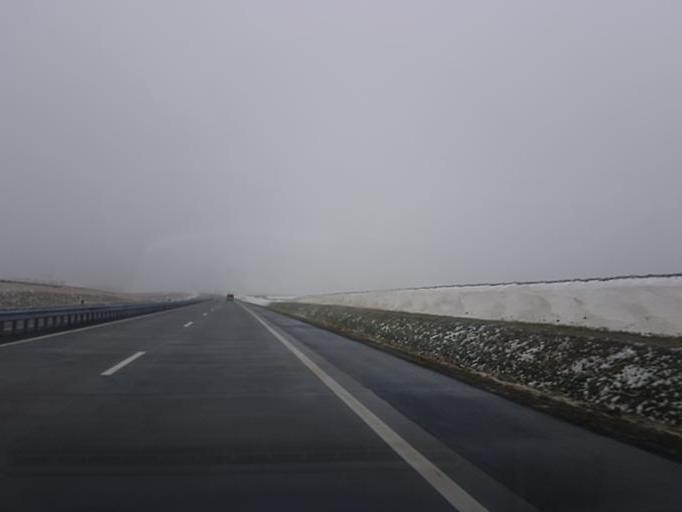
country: BY
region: Minsk
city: Atolina
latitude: 53.7435
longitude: 27.4161
